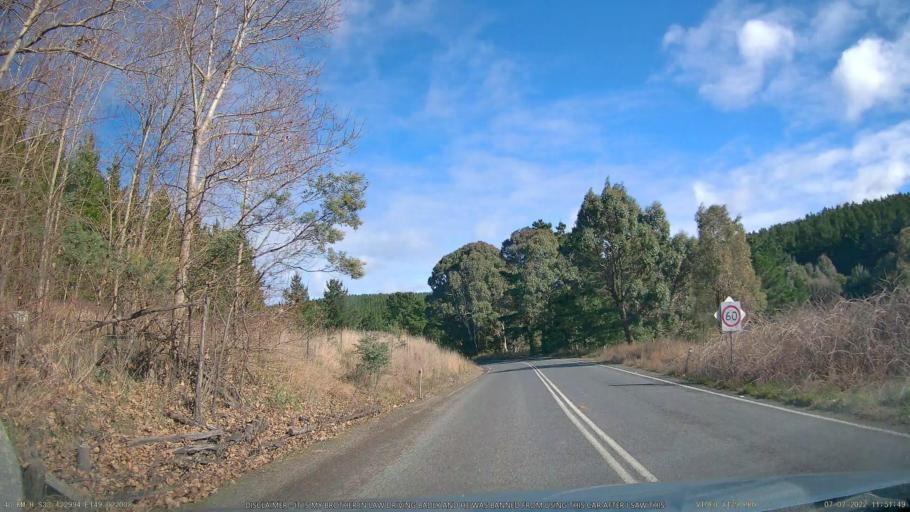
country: AU
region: New South Wales
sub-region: Orange Municipality
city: Orange
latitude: -33.4229
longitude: 149.0216
